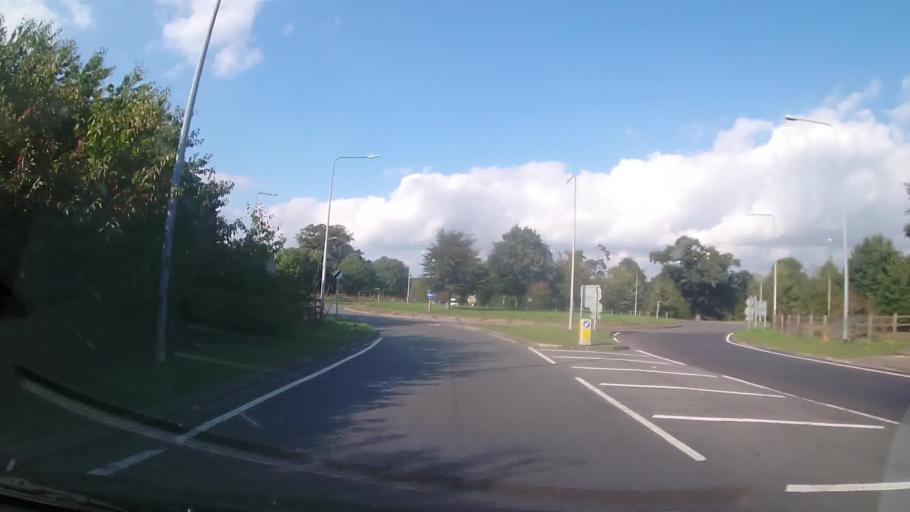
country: GB
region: England
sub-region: Kent
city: Hythe
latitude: 51.0943
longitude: 1.1028
